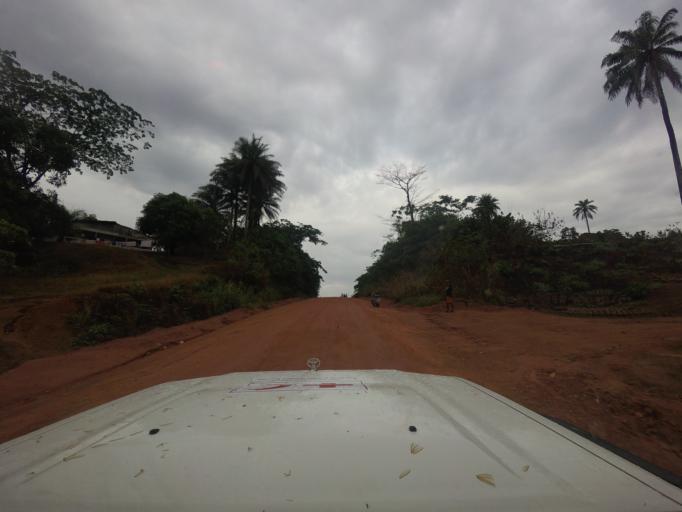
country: LR
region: Lofa
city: Voinjama
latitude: 8.4183
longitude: -9.7604
